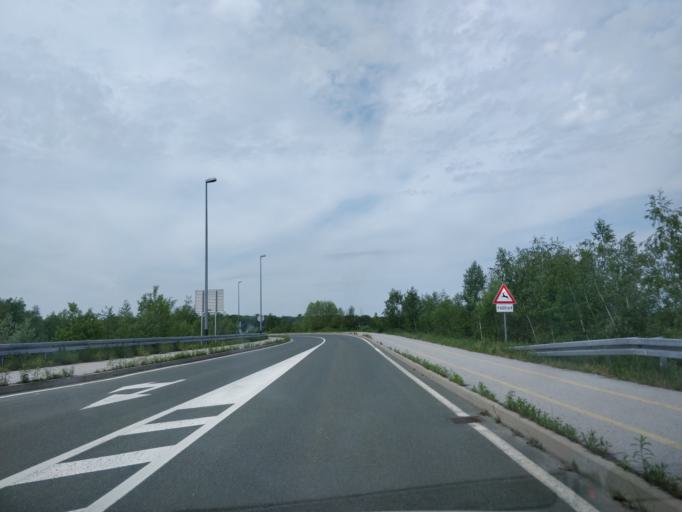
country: HR
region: Zagrebacka
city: Turopolje
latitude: 45.6237
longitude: 16.1103
